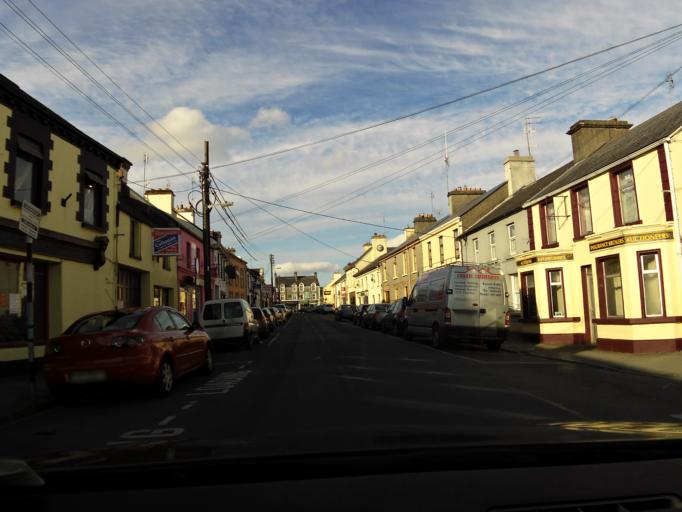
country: IE
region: Connaught
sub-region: County Galway
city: Athenry
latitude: 53.2980
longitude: -8.7488
